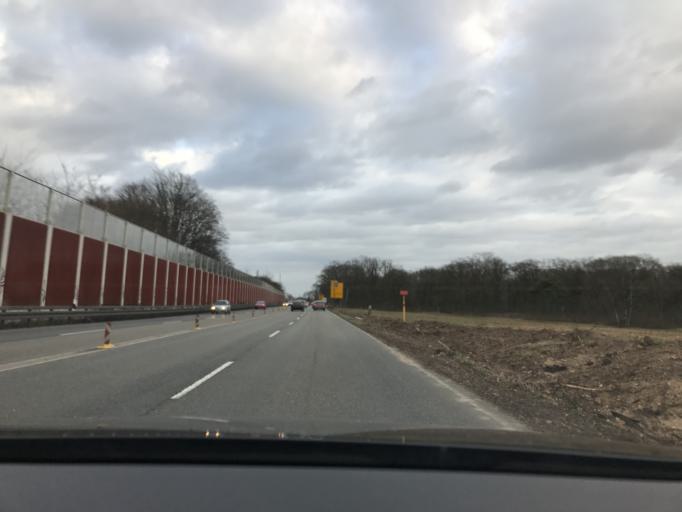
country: DE
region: North Rhine-Westphalia
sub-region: Regierungsbezirk Dusseldorf
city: Hochfeld
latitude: 51.3522
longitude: 6.7322
